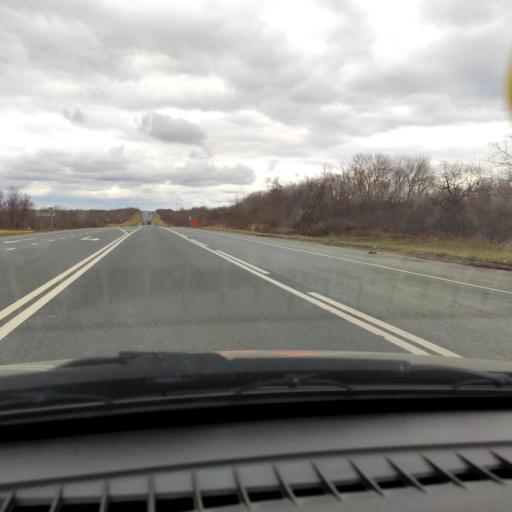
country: RU
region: Samara
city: Mezhdurechensk
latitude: 53.2579
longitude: 49.1059
